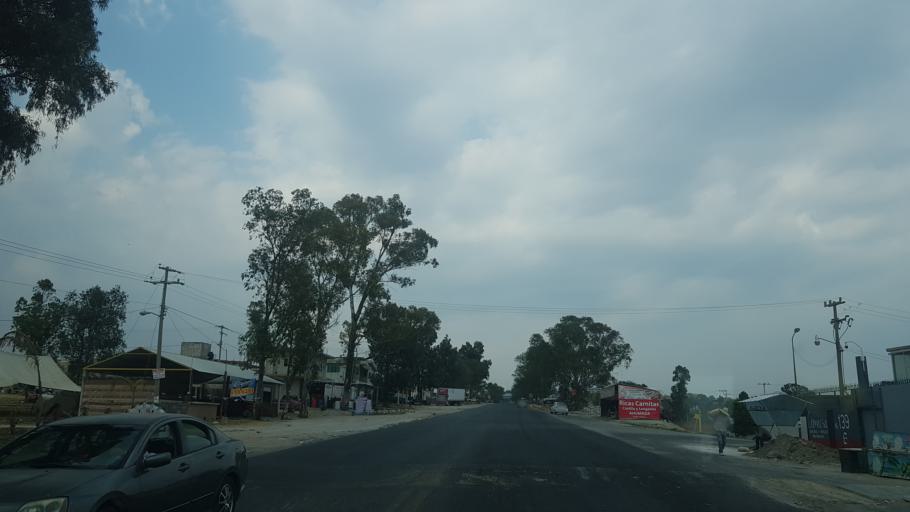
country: MX
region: Puebla
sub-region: Santa Isabel Cholula
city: San Pablo Ahuatempa
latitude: 18.9788
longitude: -98.3705
